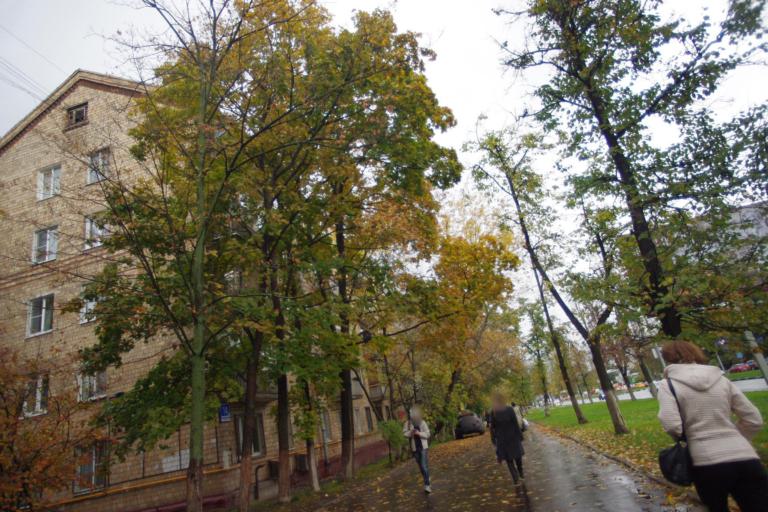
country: RU
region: Moskovskaya
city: Leninskiye Gory
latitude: 55.6910
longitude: 37.5749
